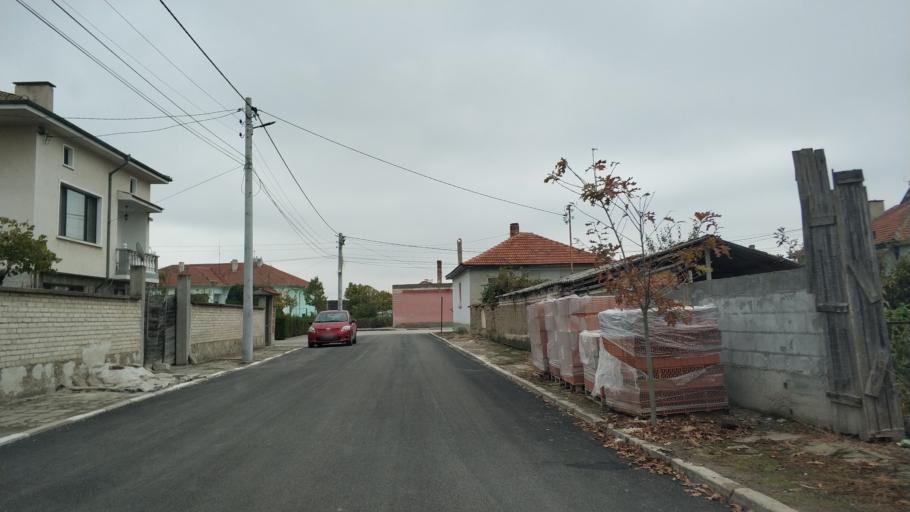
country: BG
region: Plovdiv
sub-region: Obshtina Kaloyanovo
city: Kaloyanovo
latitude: 42.3703
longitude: 24.7192
